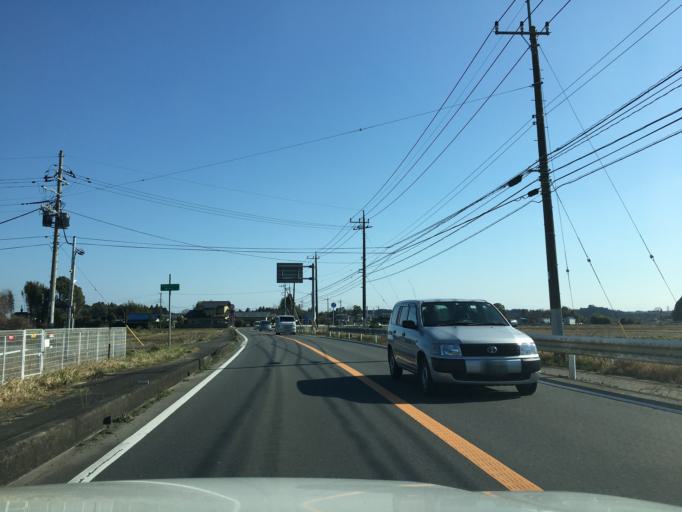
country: JP
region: Ibaraki
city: Omiya
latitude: 36.5077
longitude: 140.3714
